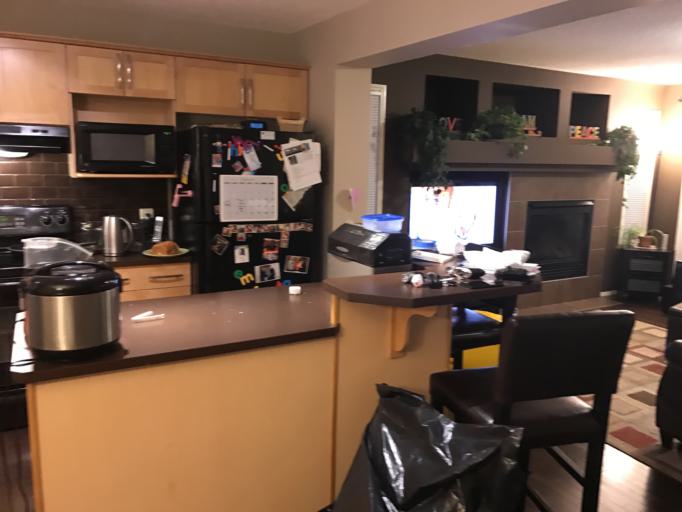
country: CA
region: Alberta
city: Chestermere
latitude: 50.9186
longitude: -113.9299
